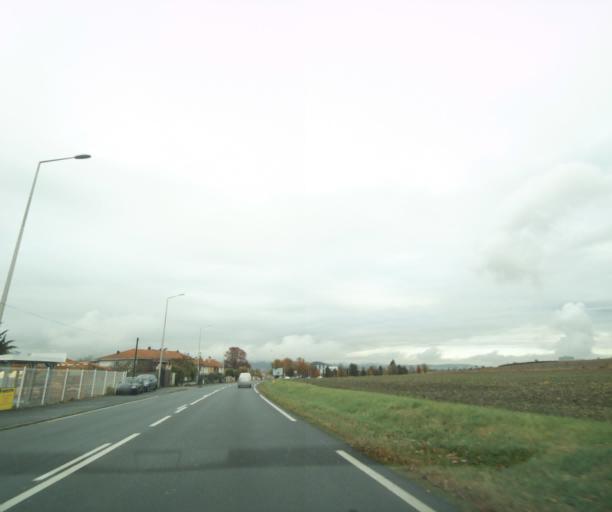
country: FR
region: Auvergne
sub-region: Departement du Puy-de-Dome
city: Perignat-les-Sarlieve
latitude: 45.7526
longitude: 3.1593
